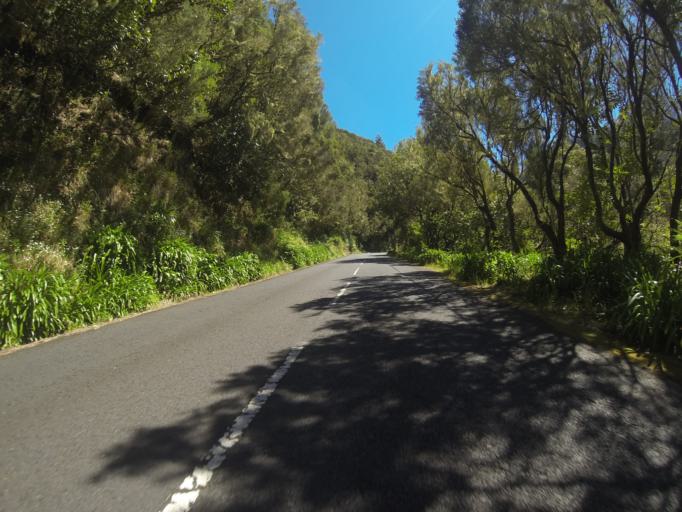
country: PT
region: Madeira
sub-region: Funchal
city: Nossa Senhora do Monte
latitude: 32.7257
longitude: -16.8889
